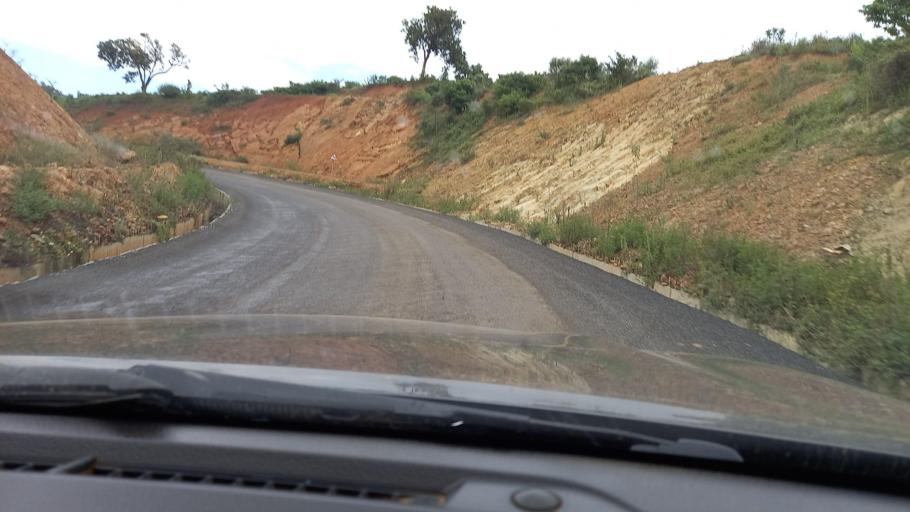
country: ET
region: Southern Nations, Nationalities, and People's Region
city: Mizan Teferi
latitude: 6.2080
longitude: 35.6562
